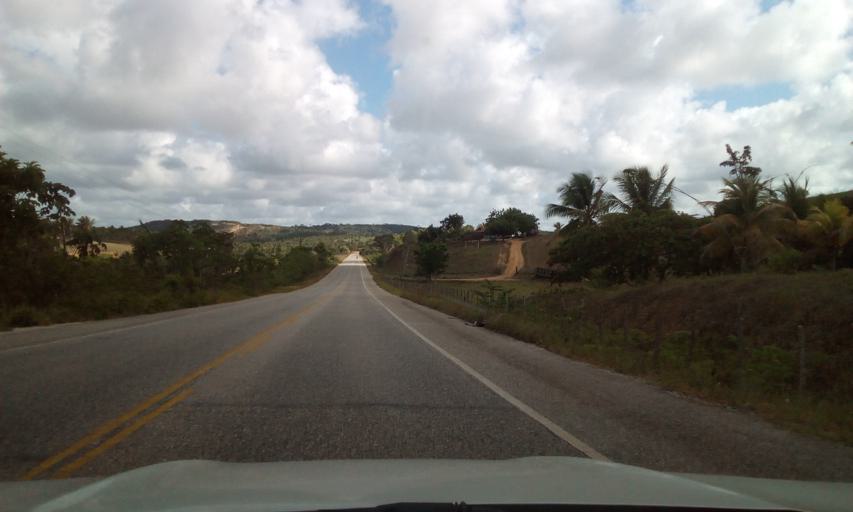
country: BR
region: Sergipe
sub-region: Indiaroba
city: Indiaroba
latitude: -11.4518
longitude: -37.4973
